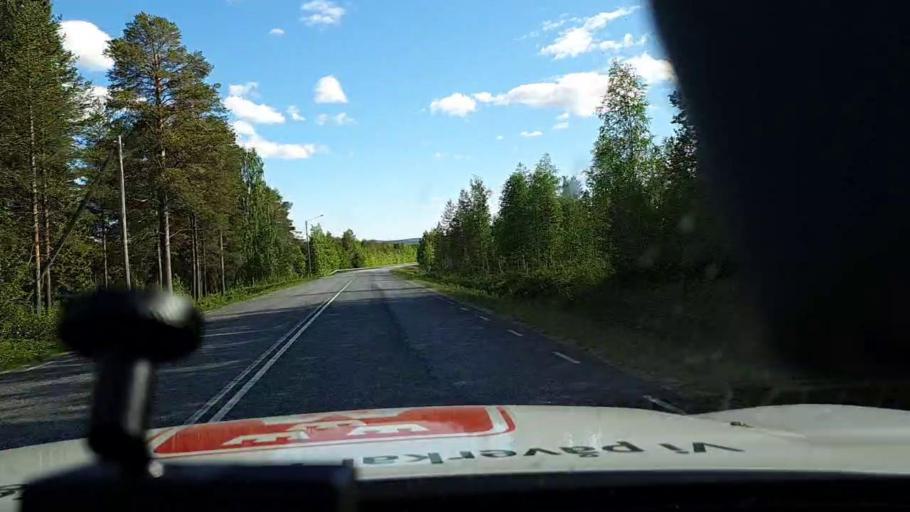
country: SE
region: Norrbotten
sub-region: Overtornea Kommun
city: OEvertornea
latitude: 66.3479
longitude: 23.6482
